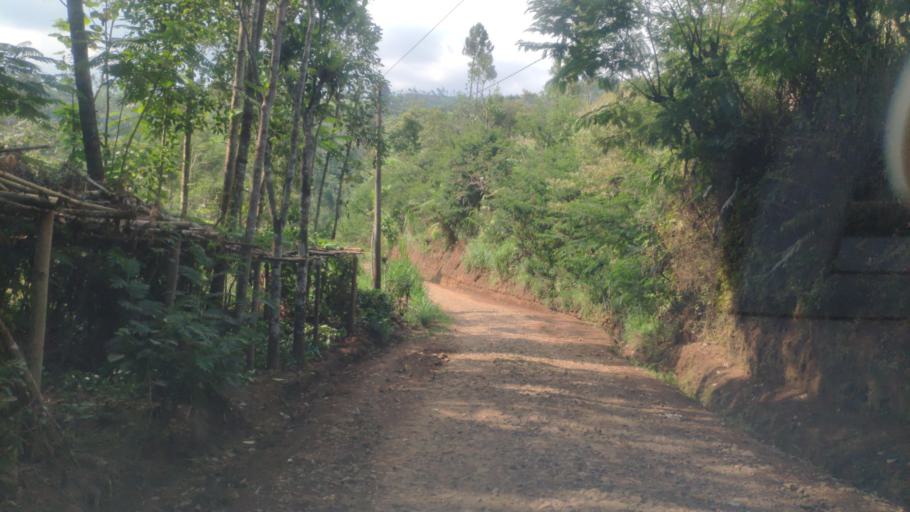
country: ID
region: Central Java
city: Buaran
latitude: -7.2425
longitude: 109.6846
